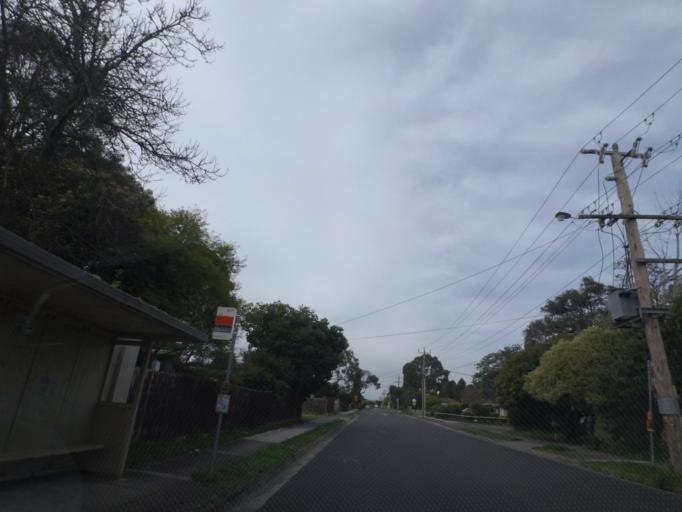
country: AU
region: Victoria
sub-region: Knox
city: Knoxfield
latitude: -37.8903
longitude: 145.2409
